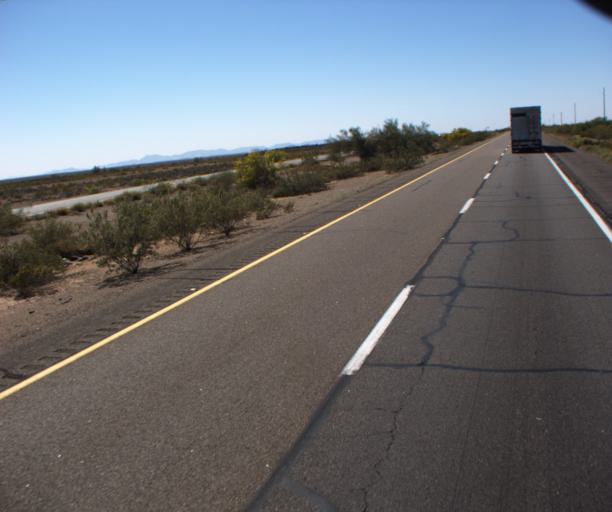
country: US
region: Arizona
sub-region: Maricopa County
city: Gila Bend
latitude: 32.8566
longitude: -113.2345
